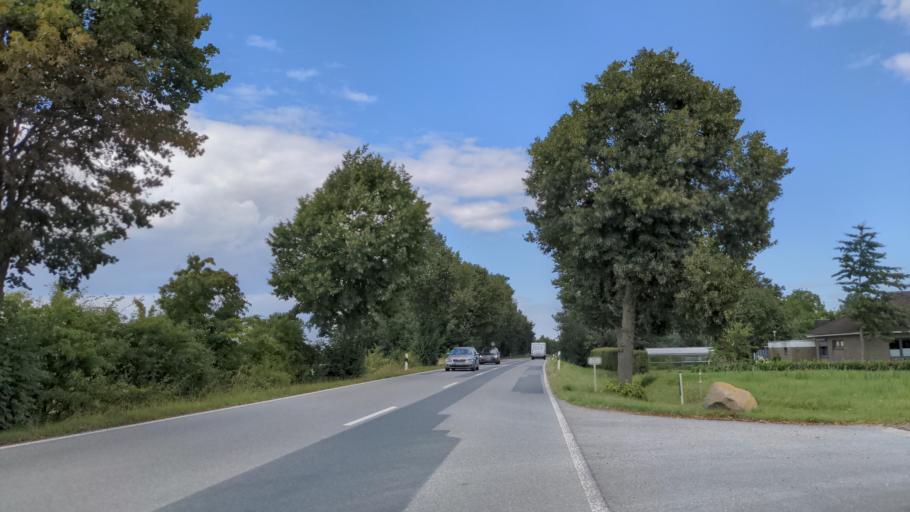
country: DE
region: Schleswig-Holstein
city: Beschendorf
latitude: 54.1724
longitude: 10.8743
